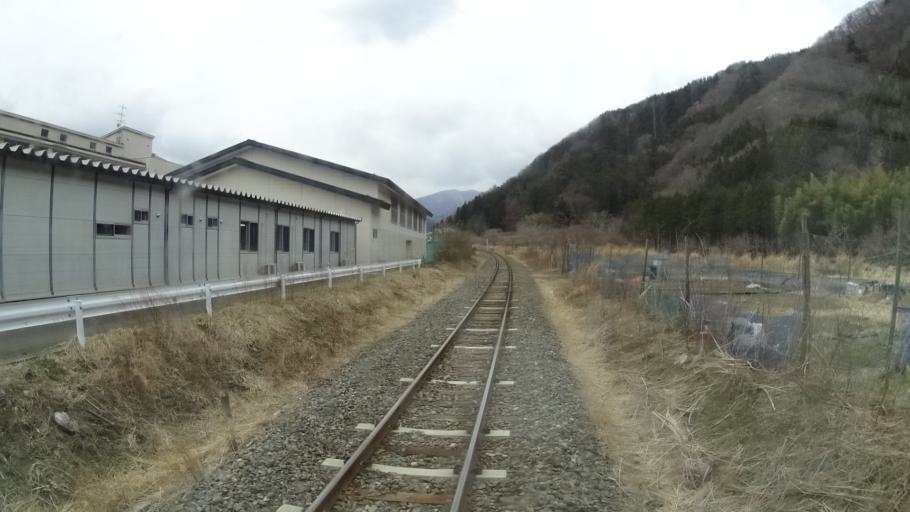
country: JP
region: Iwate
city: Kamaishi
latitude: 39.2564
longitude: 141.7983
